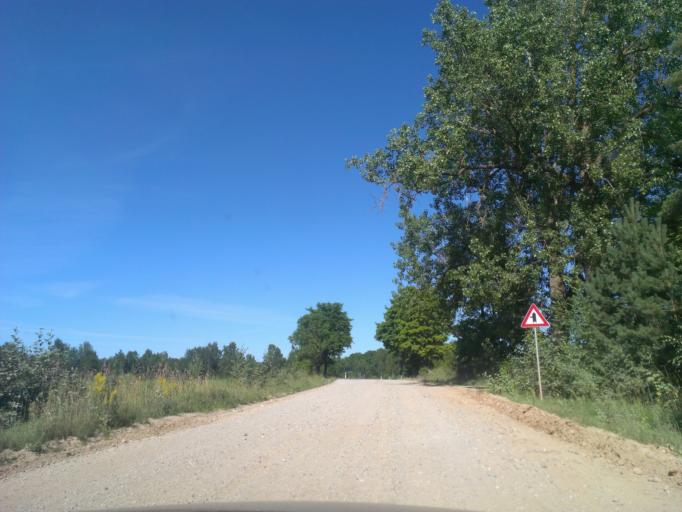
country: LV
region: Amatas Novads
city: Drabesi
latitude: 57.0636
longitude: 25.1776
